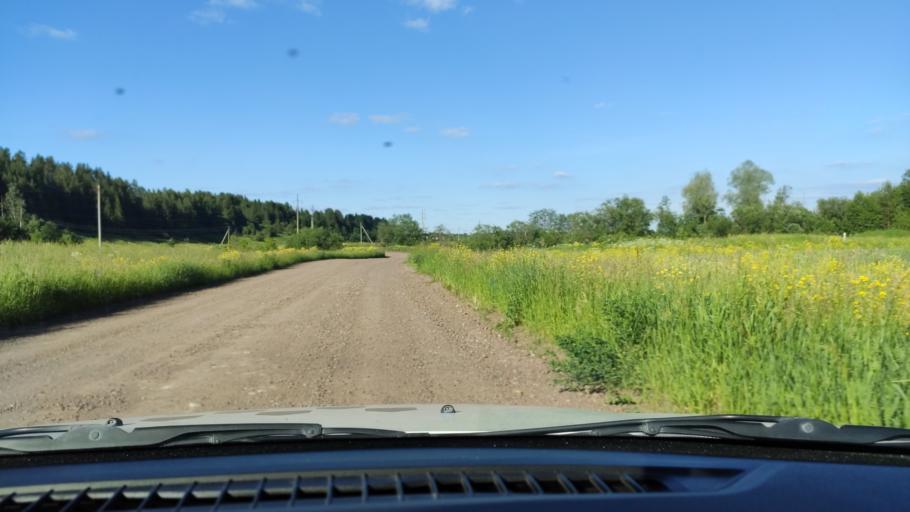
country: RU
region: Perm
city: Orda
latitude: 57.3008
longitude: 56.6273
